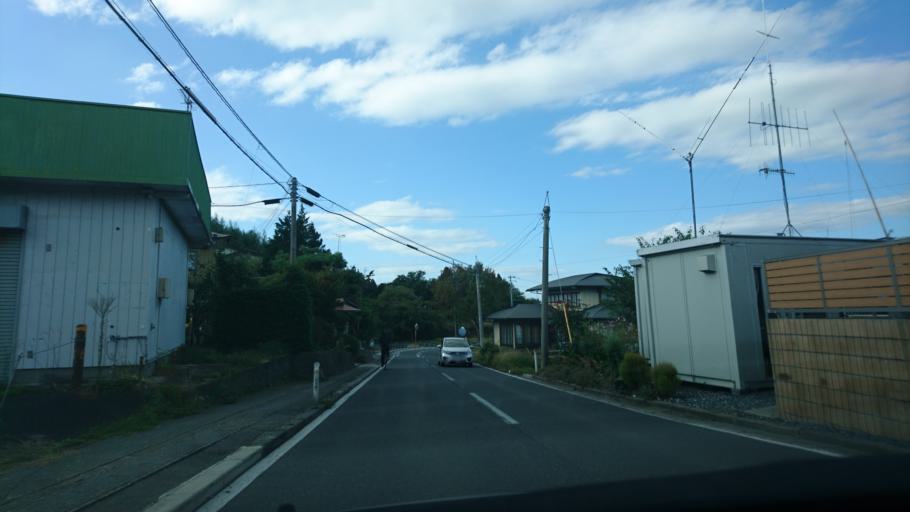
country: JP
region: Iwate
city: Ichinoseki
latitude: 38.8641
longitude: 141.3492
